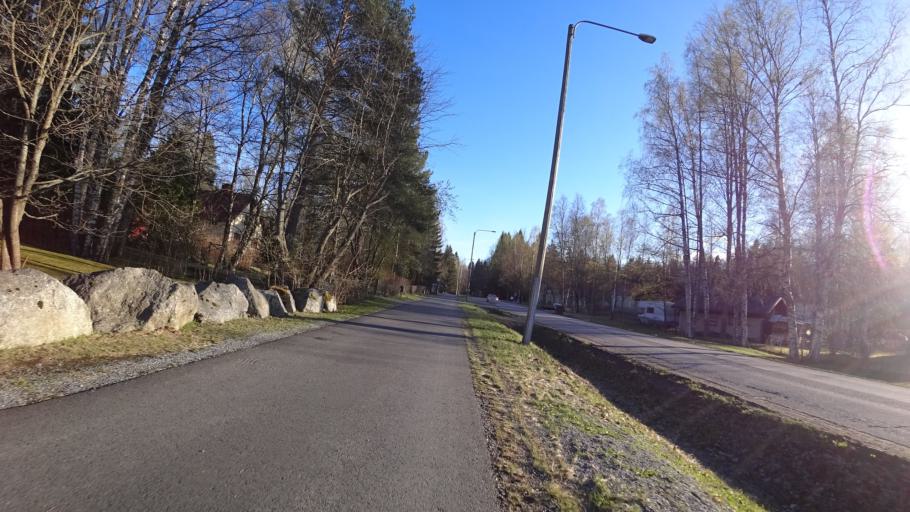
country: FI
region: Pirkanmaa
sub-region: Tampere
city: Yloejaervi
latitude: 61.5056
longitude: 23.5930
